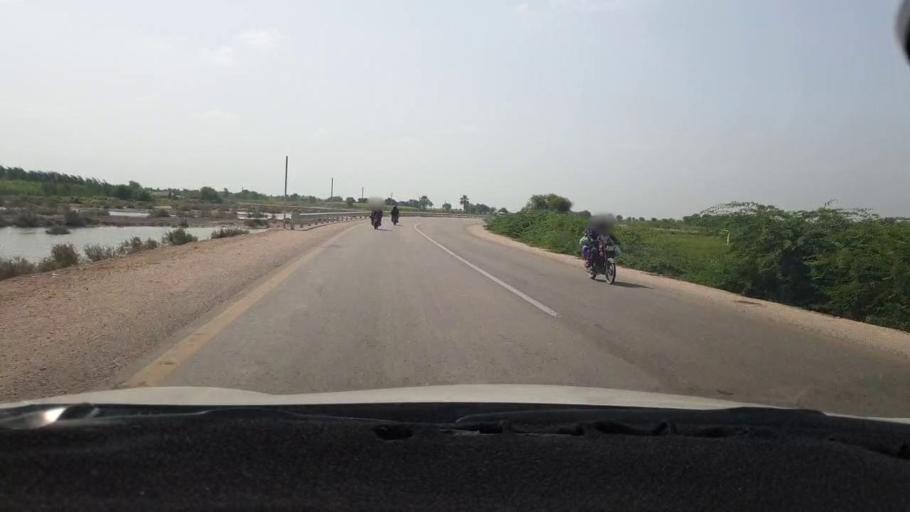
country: PK
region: Sindh
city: Mirpur Khas
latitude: 25.5889
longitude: 69.0756
